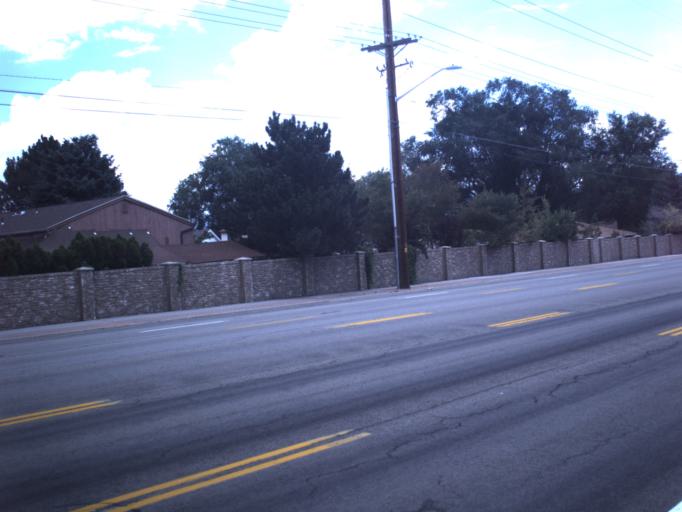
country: US
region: Utah
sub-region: Salt Lake County
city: Taylorsville
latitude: 40.6530
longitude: -111.9627
